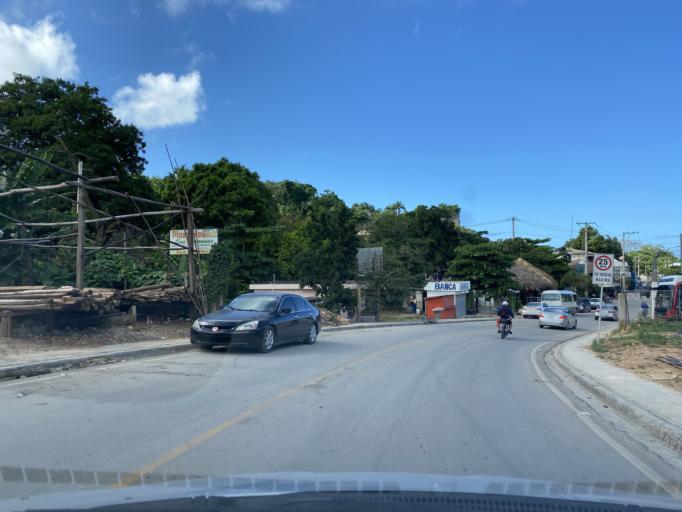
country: DO
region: Samana
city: Las Terrenas
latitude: 19.3038
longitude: -69.5491
